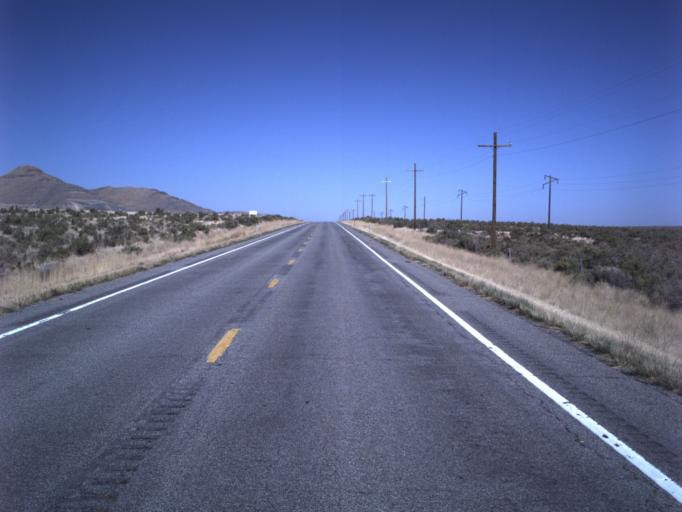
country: US
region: Utah
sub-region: Tooele County
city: Grantsville
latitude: 40.6506
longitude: -112.5318
